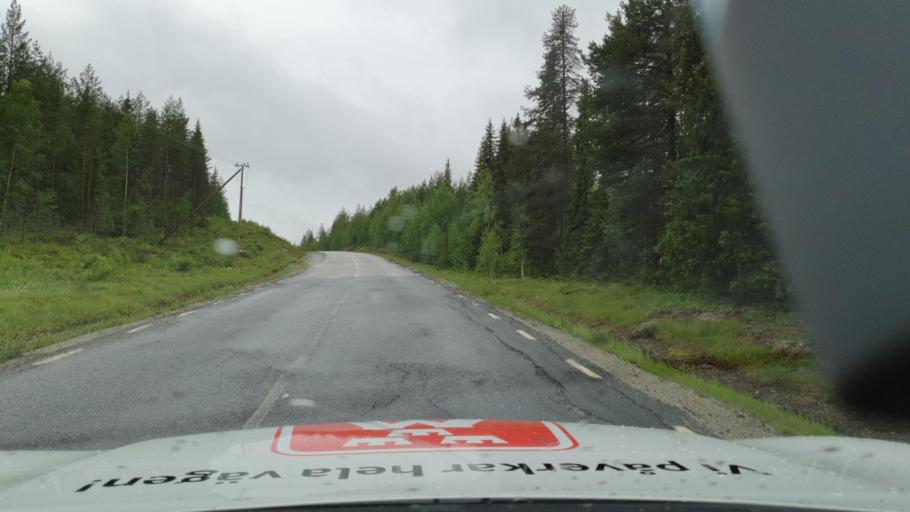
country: SE
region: Vaesterbotten
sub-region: Asele Kommun
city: Asele
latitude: 64.0061
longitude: 17.2046
